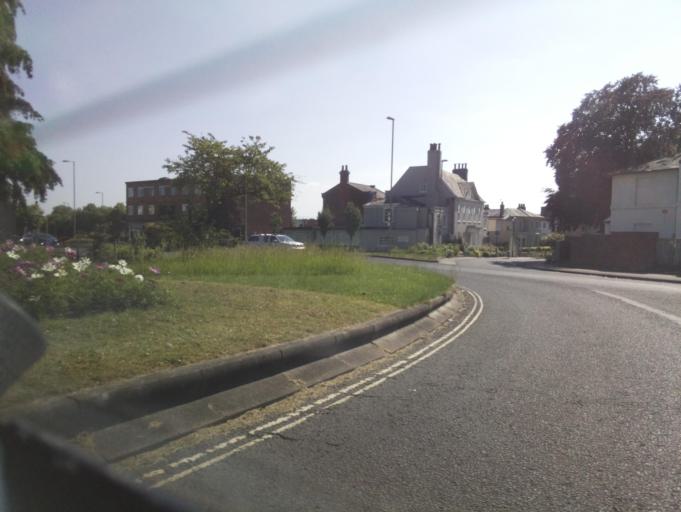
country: GB
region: England
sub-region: Hampshire
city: Andover
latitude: 51.2098
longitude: -1.4771
